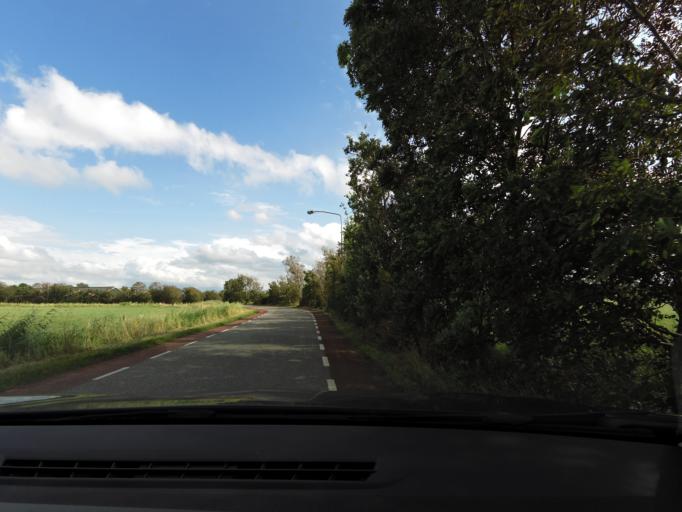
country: NL
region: South Holland
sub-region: Gemeente Goeree-Overflakkee
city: Goedereede
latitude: 51.8189
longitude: 3.9692
